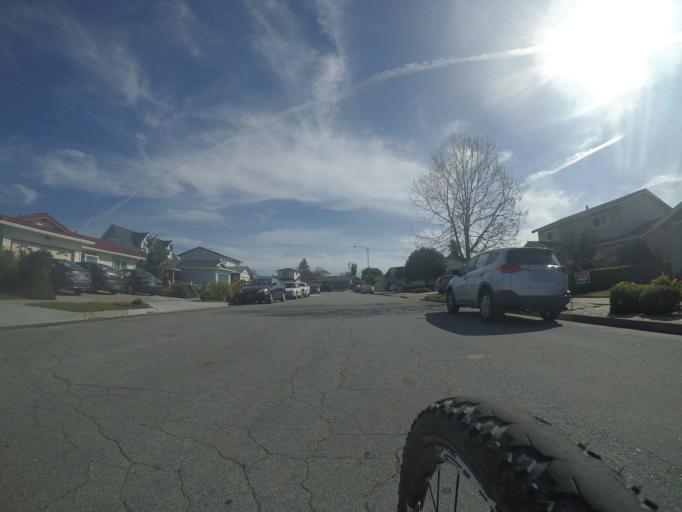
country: US
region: California
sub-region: Santa Clara County
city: Milpitas
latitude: 37.4172
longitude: -121.8673
